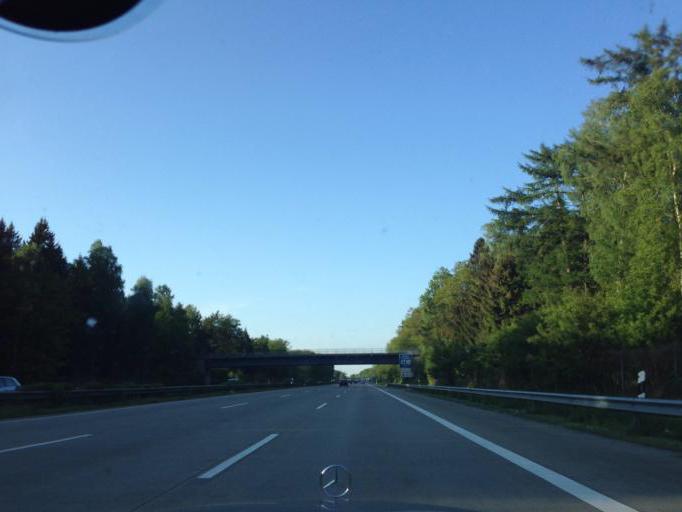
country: DE
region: Schleswig-Holstein
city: Hammoor
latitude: 53.6840
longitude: 10.3159
